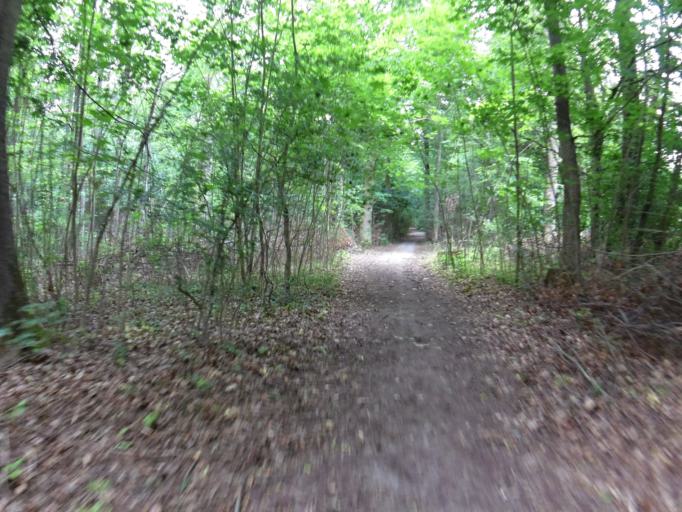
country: DE
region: Bavaria
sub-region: Regierungsbezirk Unterfranken
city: Zell am Main
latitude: 49.8203
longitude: 9.8533
